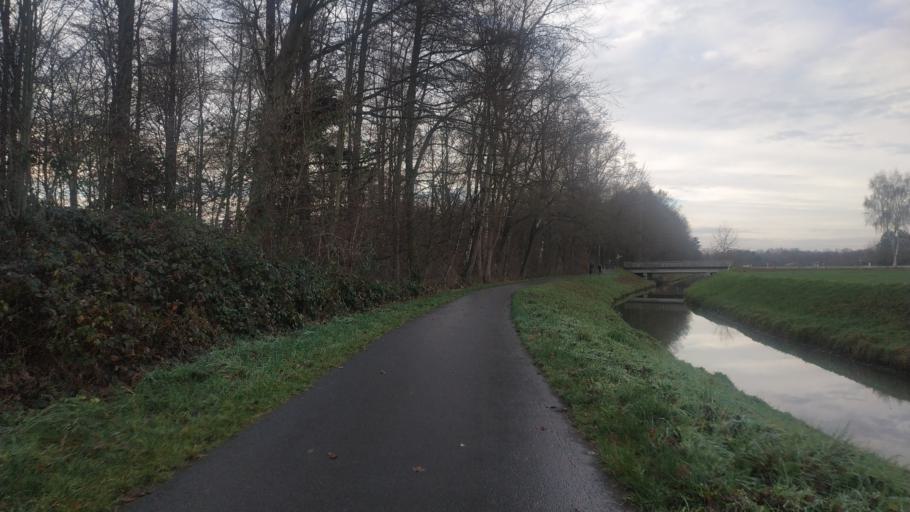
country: DE
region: North Rhine-Westphalia
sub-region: Regierungsbezirk Munster
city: Birgte
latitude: 52.2890
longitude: 7.6359
